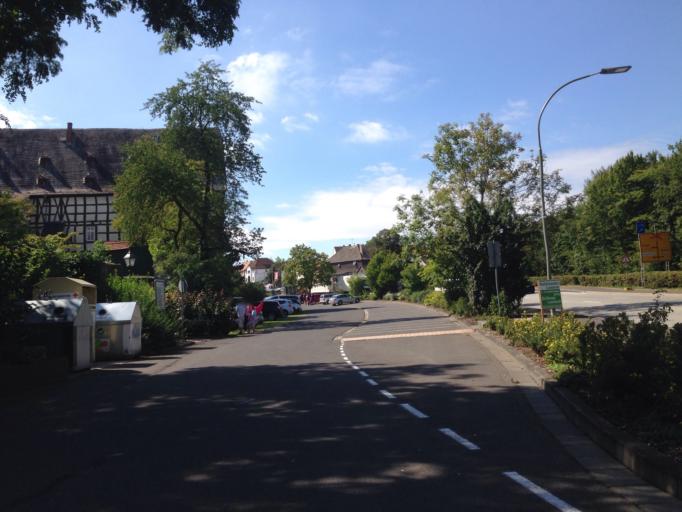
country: DE
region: Hesse
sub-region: Regierungsbezirk Giessen
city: Grunberg
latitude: 50.5935
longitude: 8.9613
